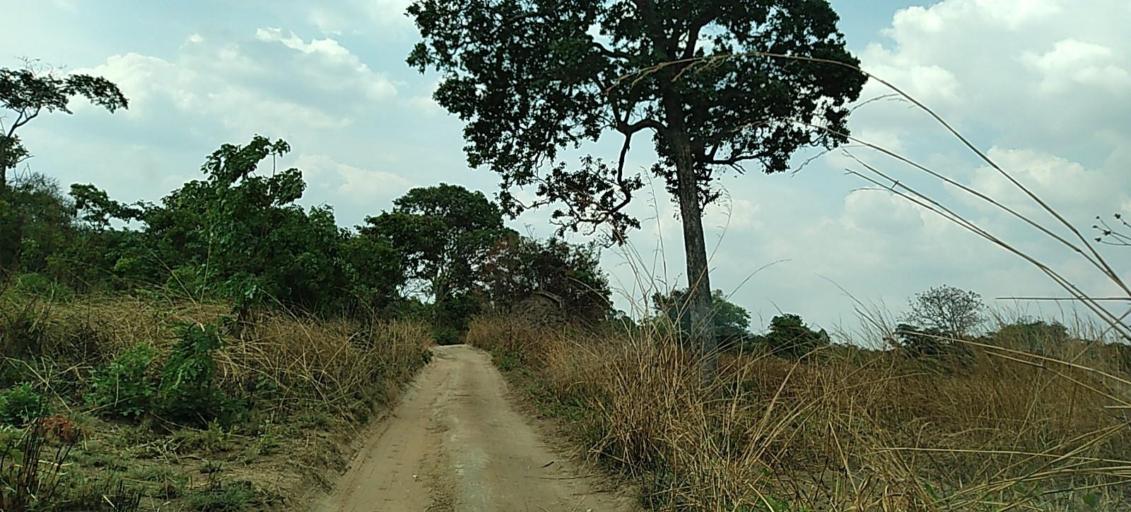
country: ZM
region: Copperbelt
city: Chililabombwe
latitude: -12.3232
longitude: 27.7487
